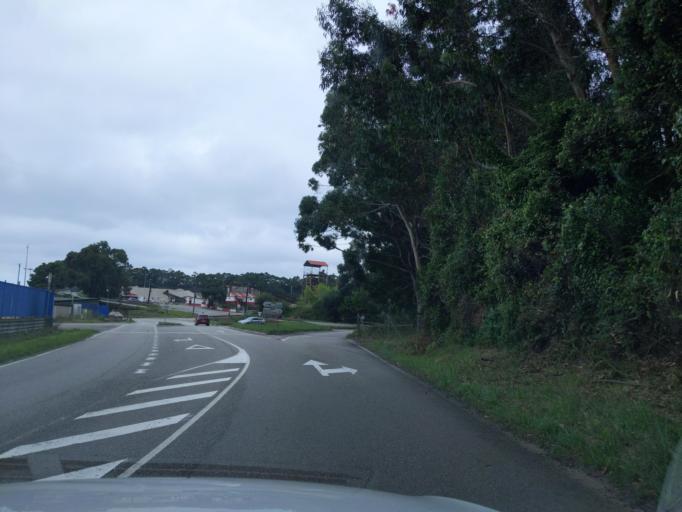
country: ES
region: Asturias
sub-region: Province of Asturias
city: Aviles
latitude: 43.5737
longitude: -5.9171
